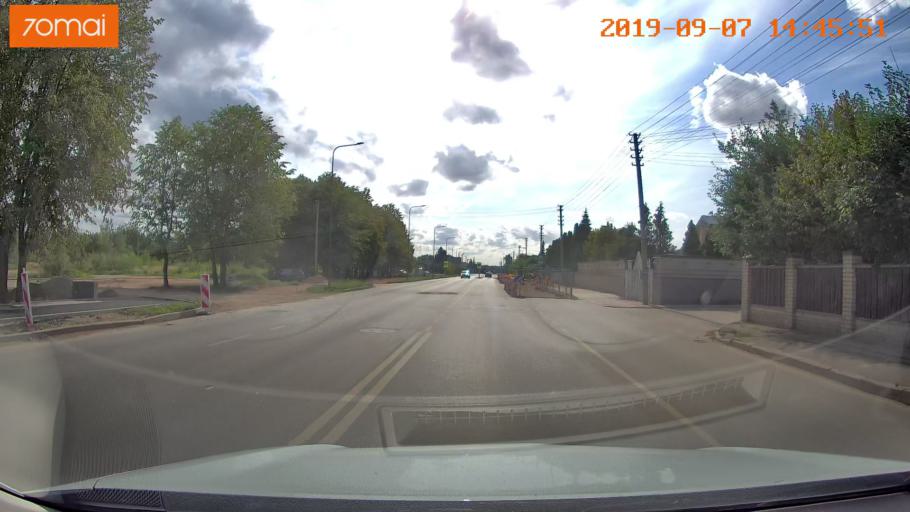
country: LT
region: Kauno apskritis
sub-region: Kaunas
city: Silainiai
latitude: 54.9300
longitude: 23.9080
